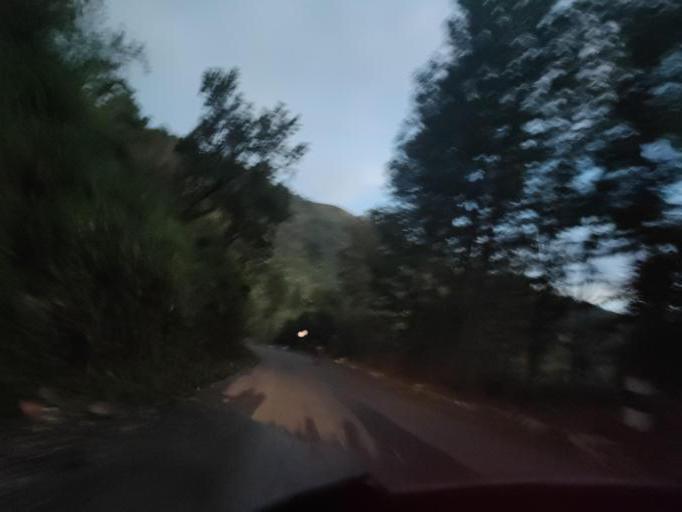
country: IN
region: Tamil Nadu
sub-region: Dindigul
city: Kodaikanal
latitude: 10.2898
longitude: 77.5365
